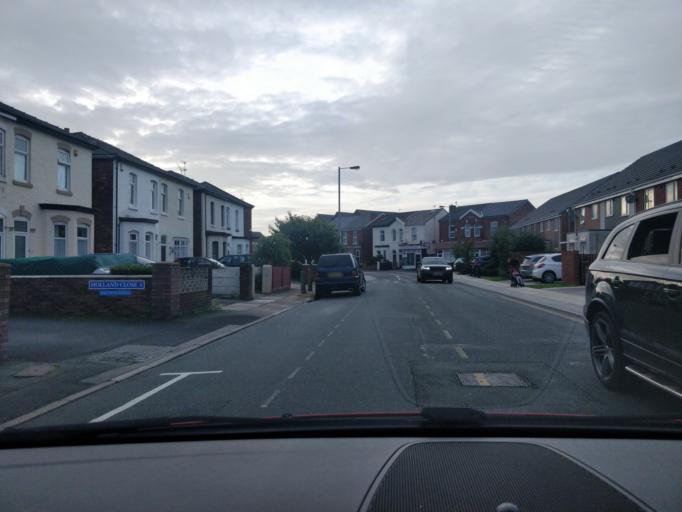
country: GB
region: England
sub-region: Sefton
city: Southport
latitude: 53.6433
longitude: -2.9970
